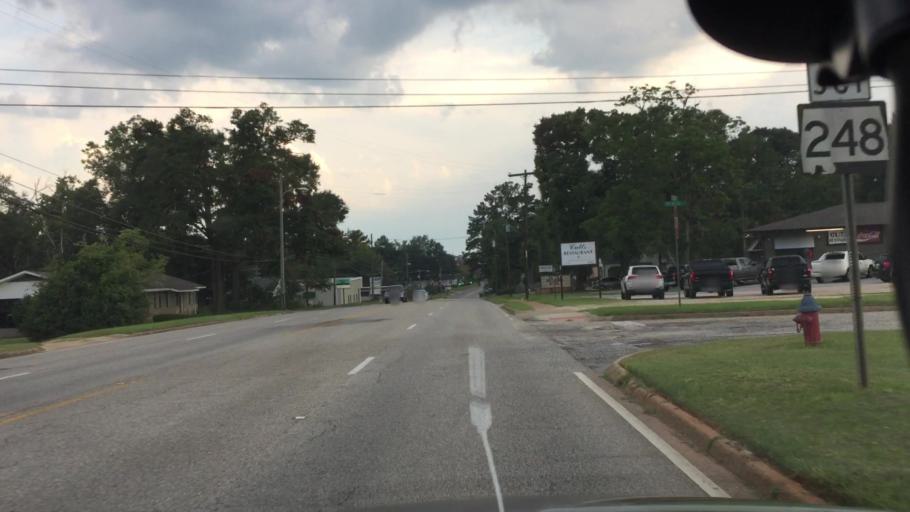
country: US
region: Alabama
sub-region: Coffee County
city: Enterprise
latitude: 31.3195
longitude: -85.8498
